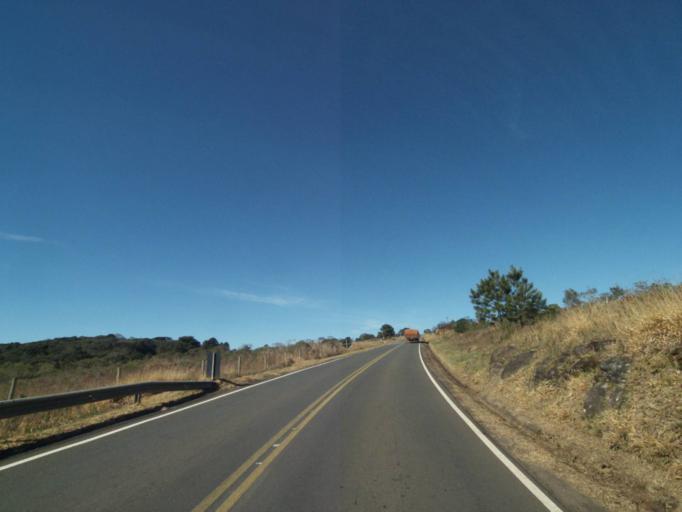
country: BR
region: Parana
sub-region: Tibagi
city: Tibagi
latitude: -24.6160
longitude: -50.2537
